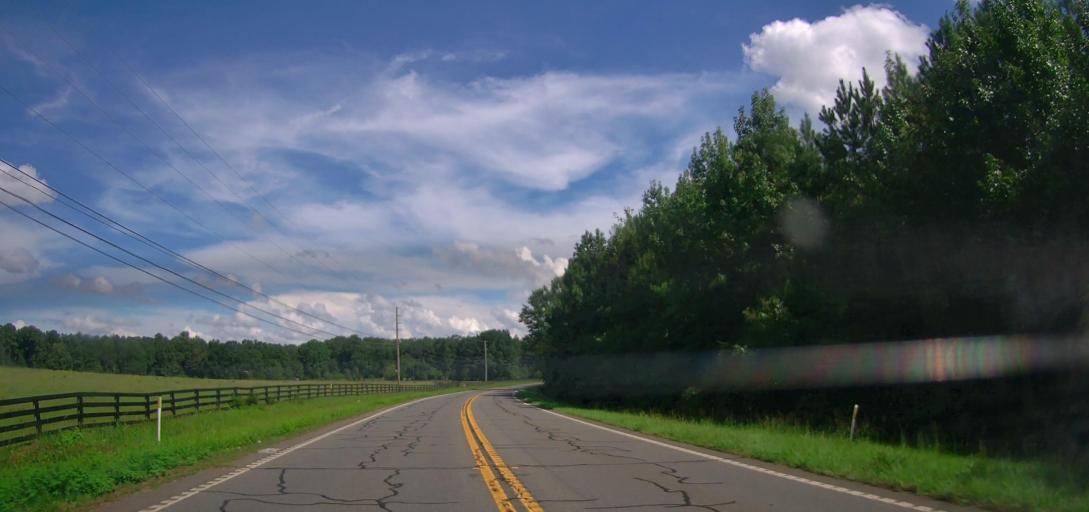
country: US
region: Georgia
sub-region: Talbot County
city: Sardis
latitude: 32.7973
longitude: -84.5716
